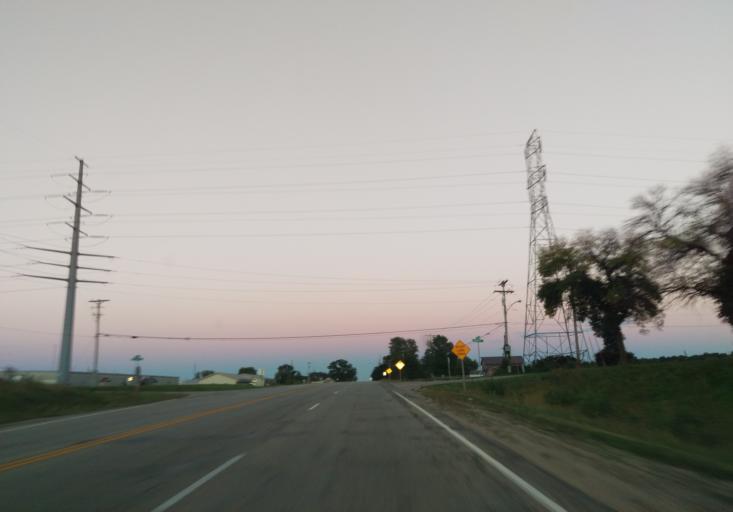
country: US
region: Wisconsin
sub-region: Rock County
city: Janesville
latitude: 42.7301
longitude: -89.0488
